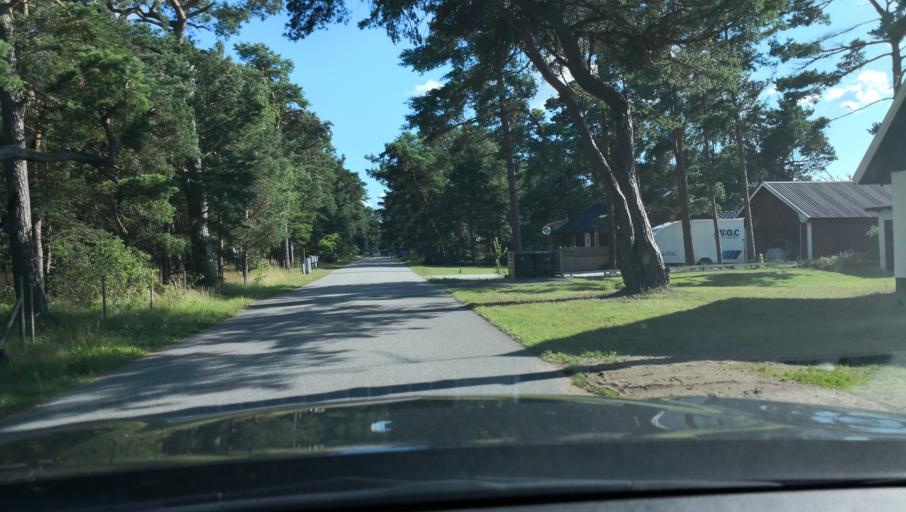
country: SE
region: Skane
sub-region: Simrishamns Kommun
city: Kivik
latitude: 55.7714
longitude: 14.1963
